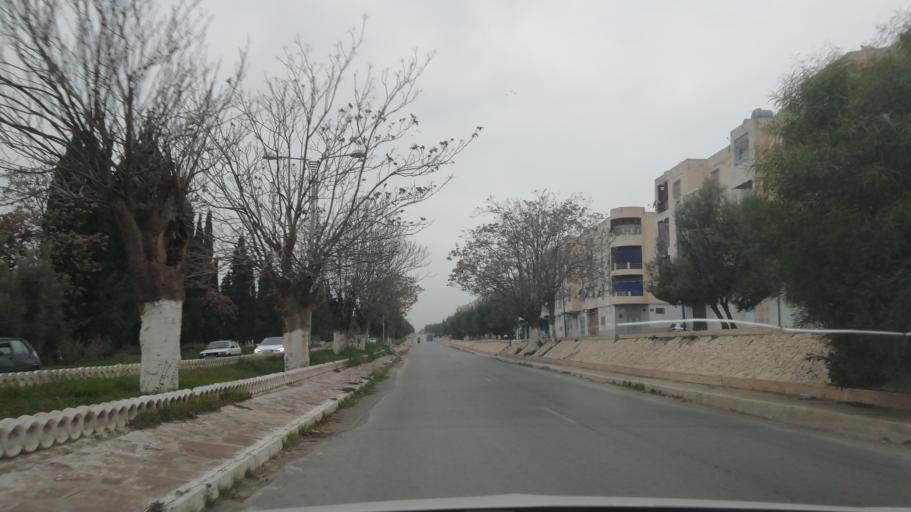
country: DZ
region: Sidi Bel Abbes
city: Sfizef
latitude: 35.2315
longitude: -0.2543
